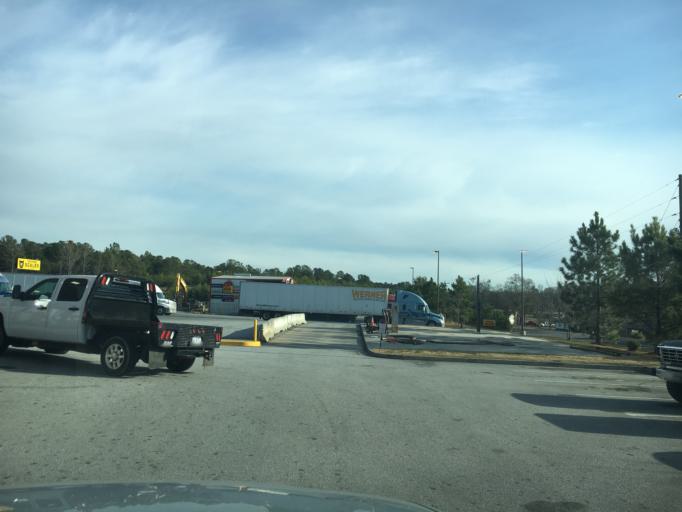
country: US
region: Georgia
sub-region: Hart County
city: Reed Creek
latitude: 34.5046
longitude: -82.9616
